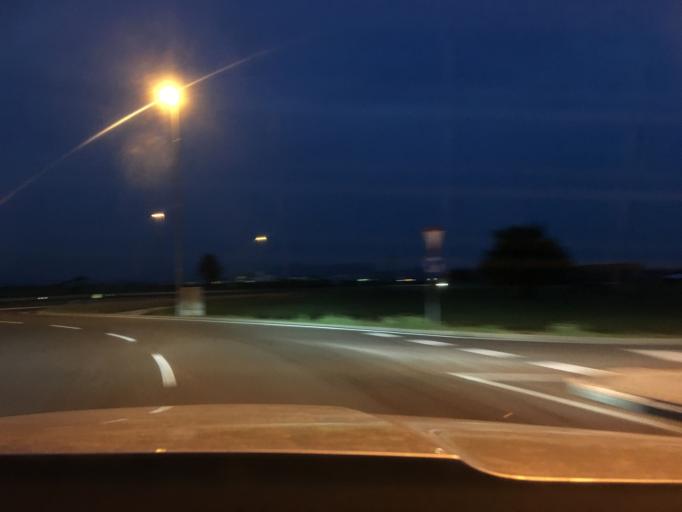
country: SI
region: Menges
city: Menges
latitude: 46.1734
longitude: 14.5765
